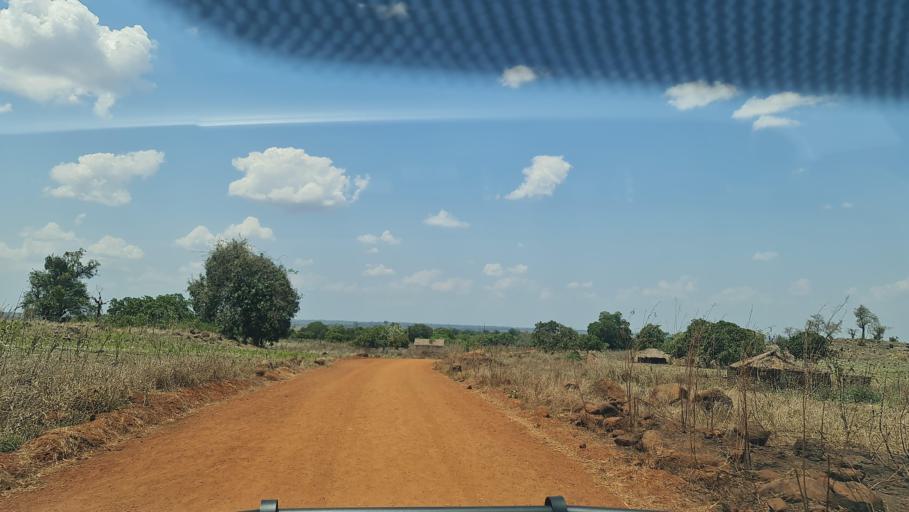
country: MZ
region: Nampula
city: Nacala
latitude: -14.7976
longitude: 40.0697
